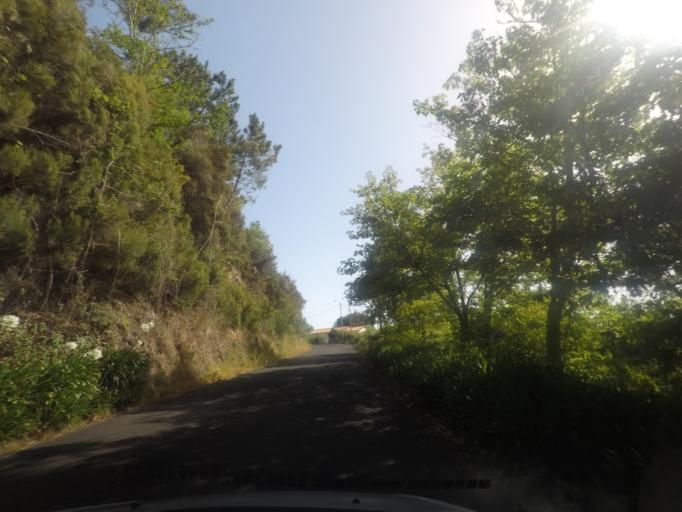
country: PT
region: Madeira
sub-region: Calheta
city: Estreito da Calheta
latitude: 32.7608
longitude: -17.2018
